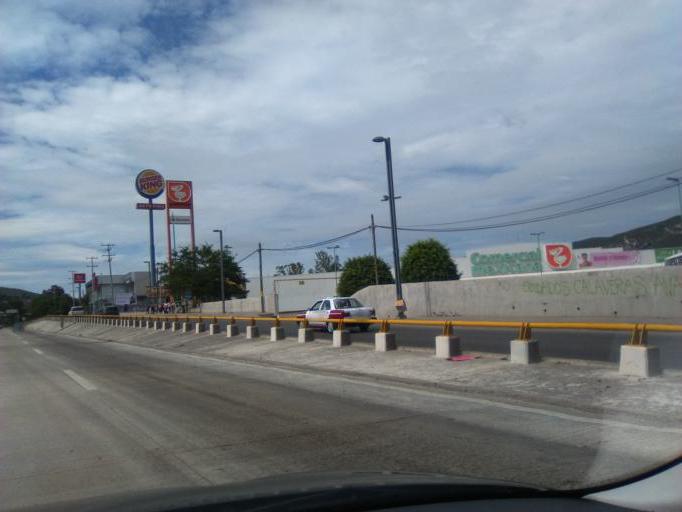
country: MX
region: Guerrero
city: Chilpancingo de los Bravos
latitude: 17.5418
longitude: -99.5032
